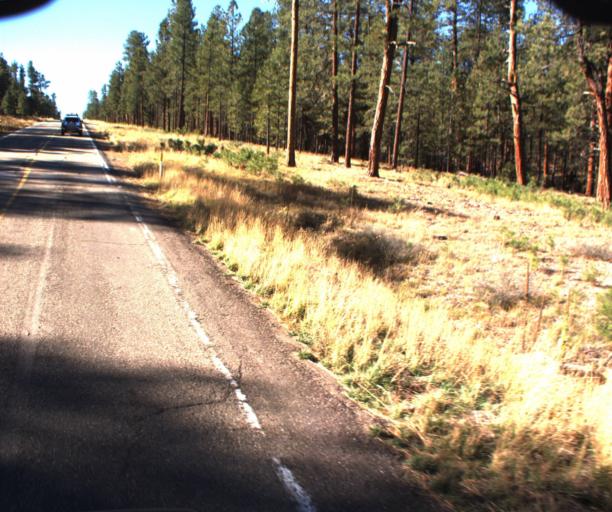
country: US
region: Arizona
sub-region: Coconino County
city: Fredonia
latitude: 36.7294
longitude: -112.1962
